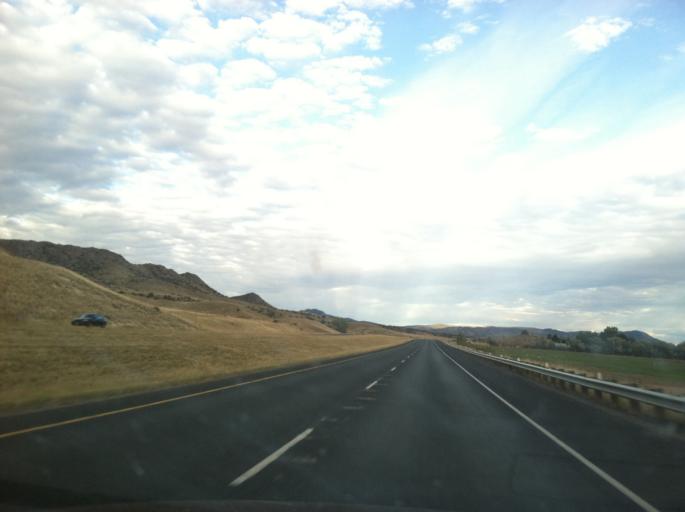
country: US
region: Montana
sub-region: Jefferson County
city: Whitehall
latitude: 45.8764
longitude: -112.0686
